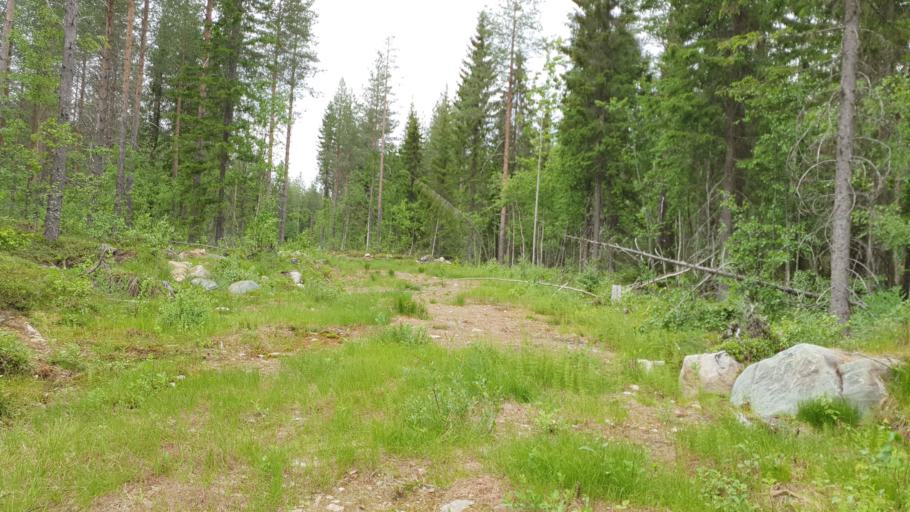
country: FI
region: Kainuu
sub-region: Kehys-Kainuu
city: Kuhmo
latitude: 64.4431
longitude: 29.6867
